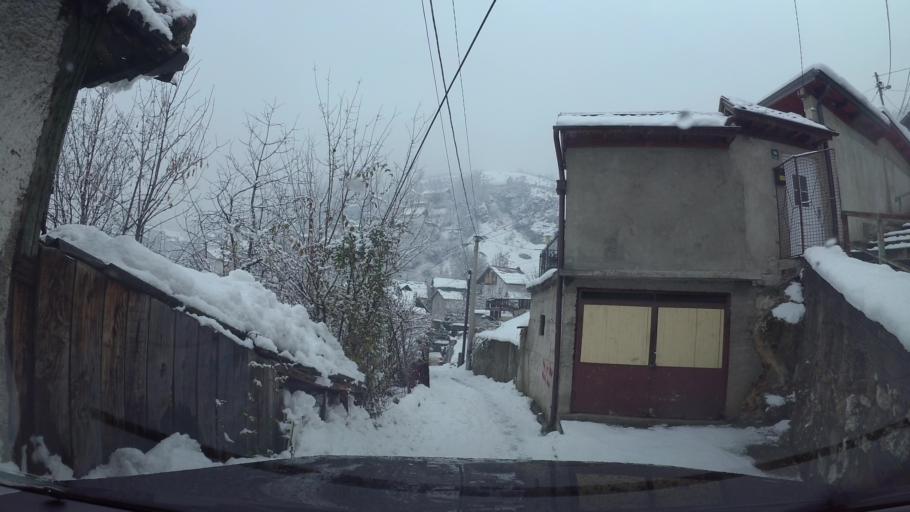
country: BA
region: Federation of Bosnia and Herzegovina
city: Kobilja Glava
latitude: 43.8495
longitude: 18.4302
